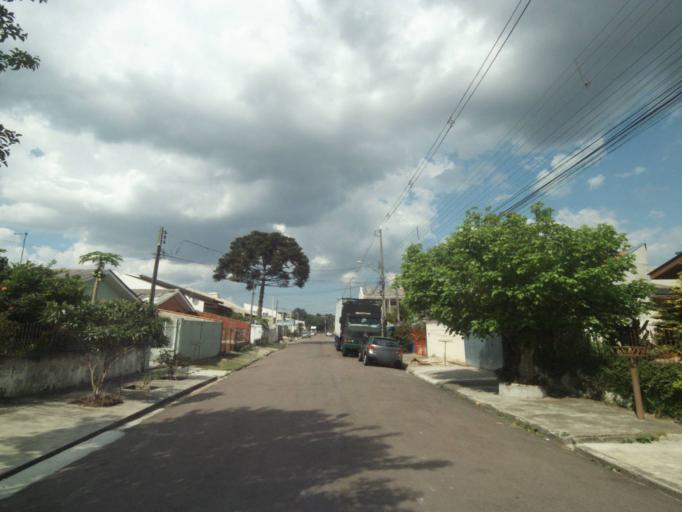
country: BR
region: Parana
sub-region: Sao Jose Dos Pinhais
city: Sao Jose dos Pinhais
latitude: -25.5293
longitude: -49.2636
